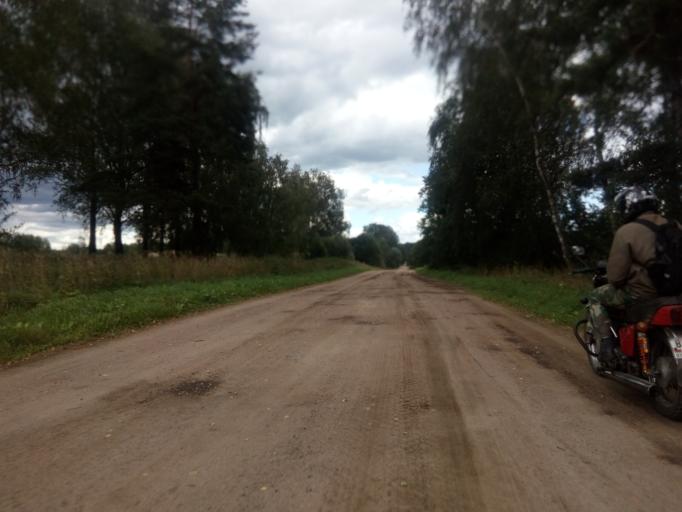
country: BY
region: Vitebsk
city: Dzisna
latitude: 55.7071
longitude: 28.3205
